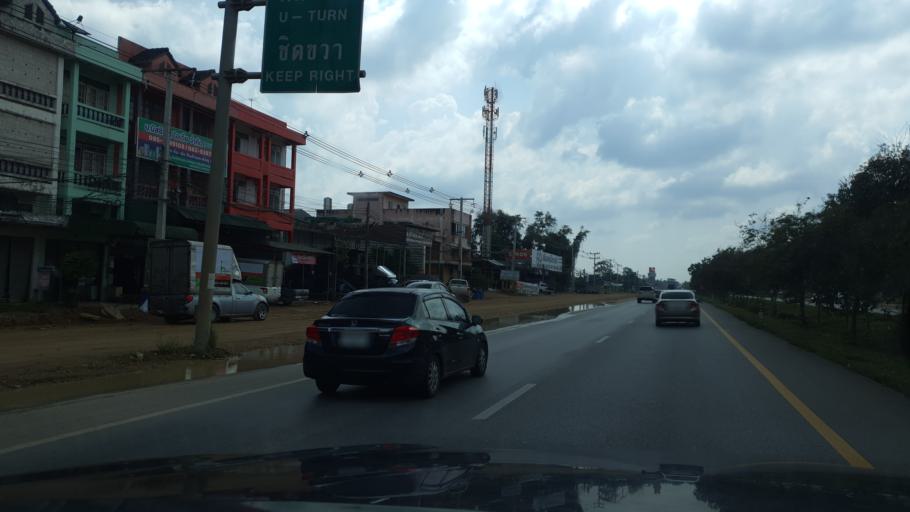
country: TH
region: Chumphon
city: Chumphon
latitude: 10.4883
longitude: 99.1231
